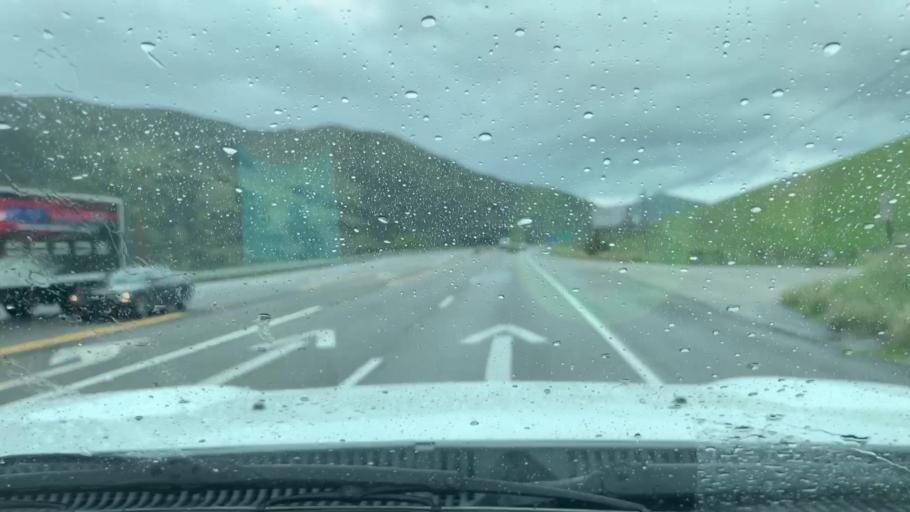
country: US
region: California
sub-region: San Luis Obispo County
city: San Luis Obispo
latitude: 35.2961
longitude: -120.6299
